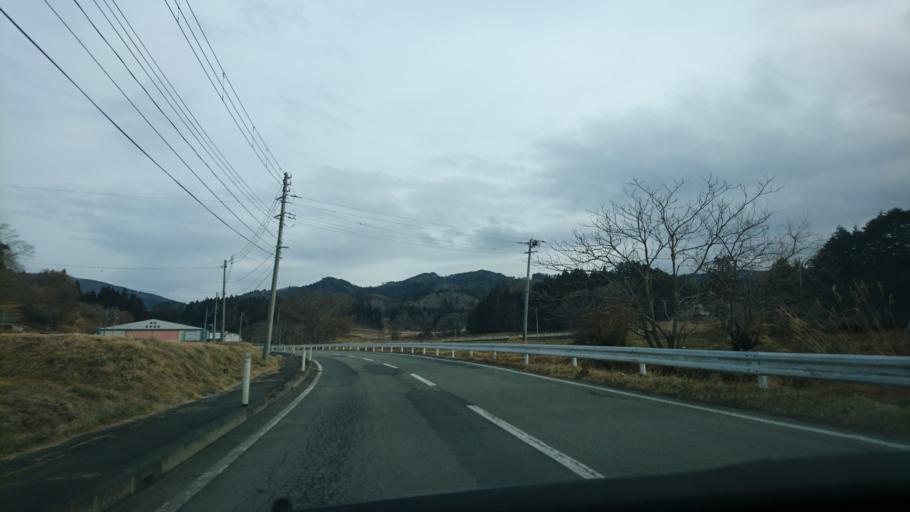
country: JP
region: Iwate
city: Ichinoseki
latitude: 38.8450
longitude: 141.3762
